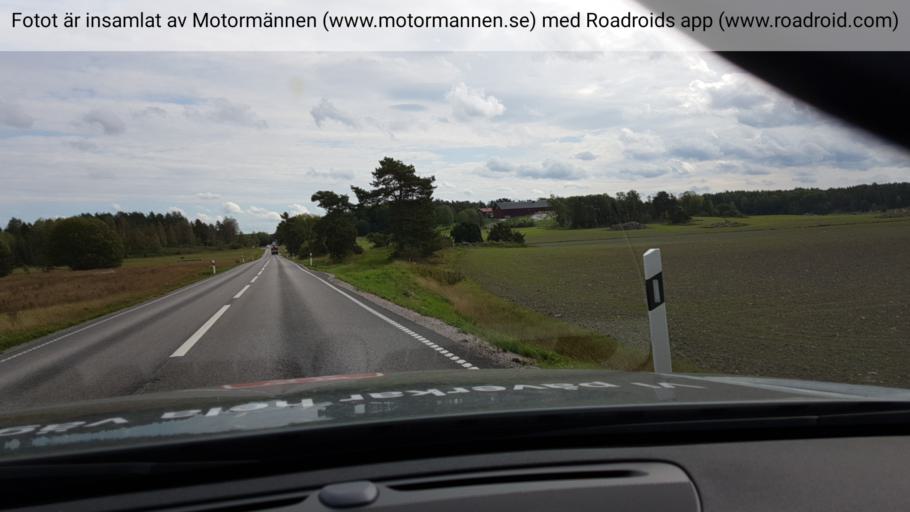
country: SE
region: Stockholm
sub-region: Norrtalje Kommun
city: Nykvarn
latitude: 59.7452
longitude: 18.1112
